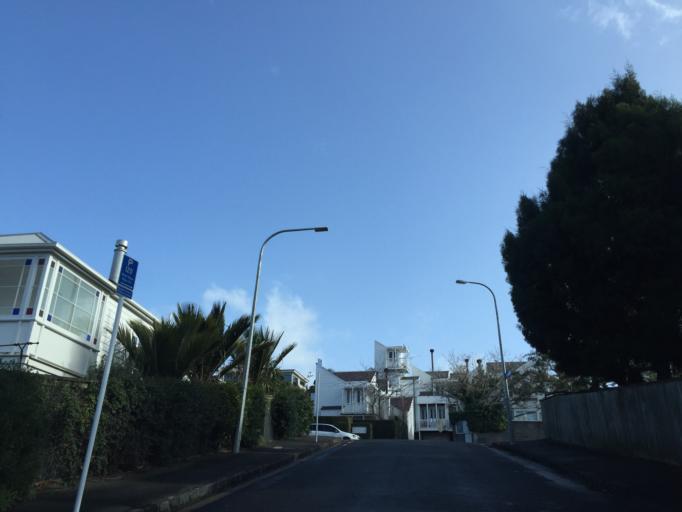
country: NZ
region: Auckland
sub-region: Auckland
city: Auckland
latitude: -36.8515
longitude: 174.7472
